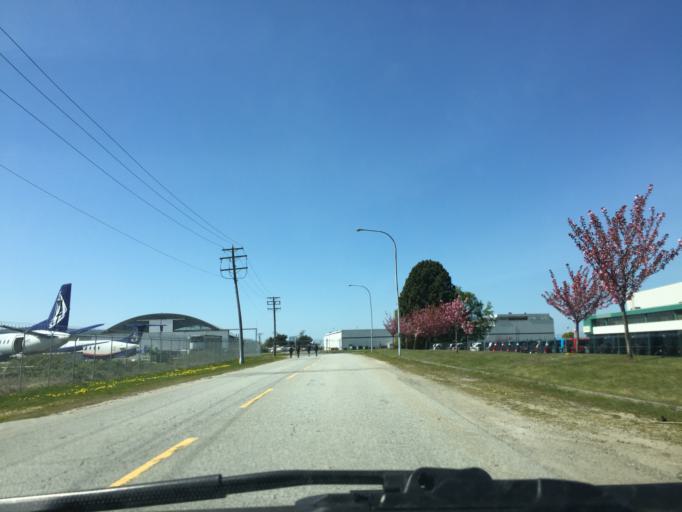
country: CA
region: British Columbia
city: Richmond
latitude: 49.1801
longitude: -123.1603
